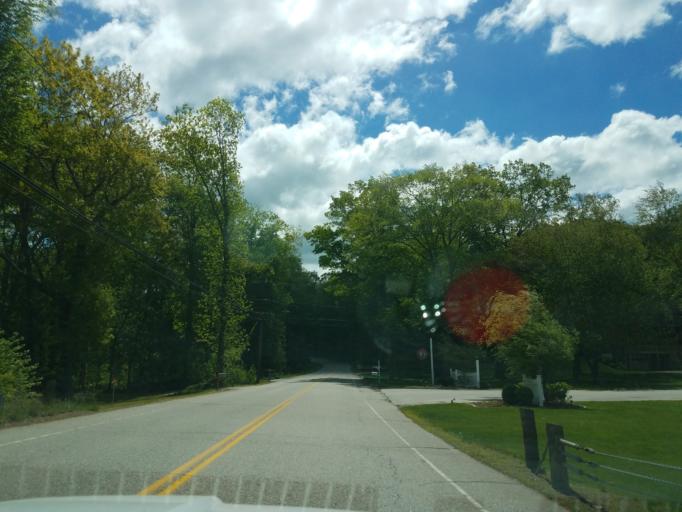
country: US
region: Connecticut
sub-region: New London County
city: Colchester
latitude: 41.5006
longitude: -72.2970
